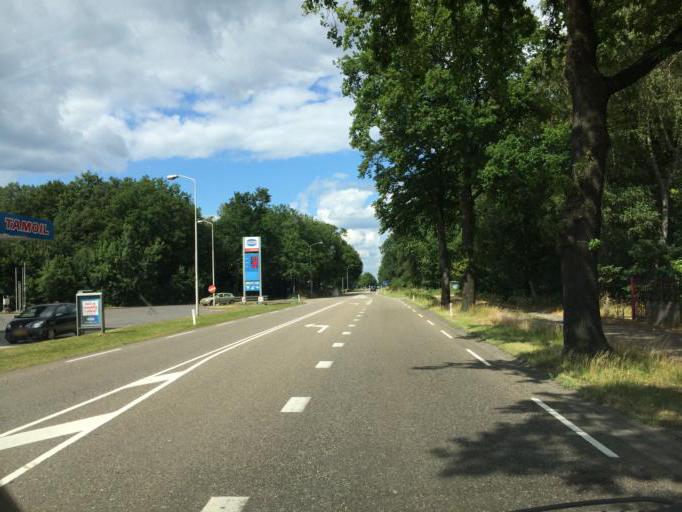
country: BE
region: Flanders
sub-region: Provincie Limburg
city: Neerpelt
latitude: 51.2701
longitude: 5.3983
